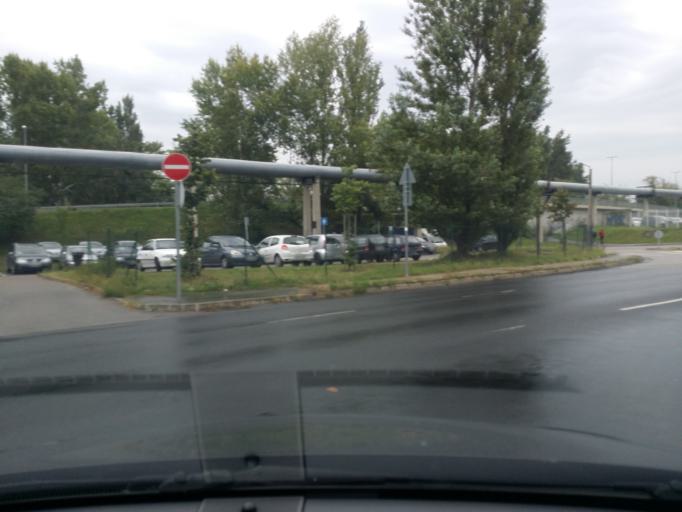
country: HU
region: Budapest
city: Budapest XV. keruelet
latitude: 47.5711
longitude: 19.1123
